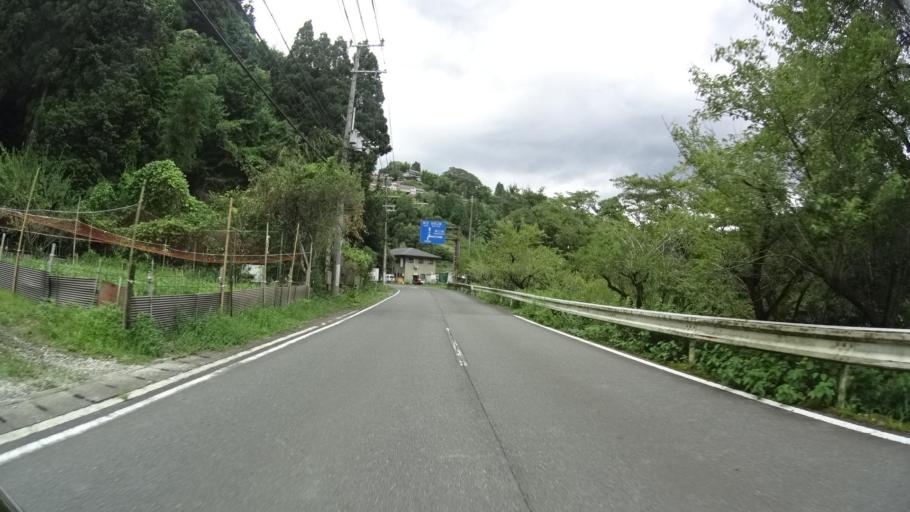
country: JP
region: Mie
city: Nabari
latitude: 34.7064
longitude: 136.0118
